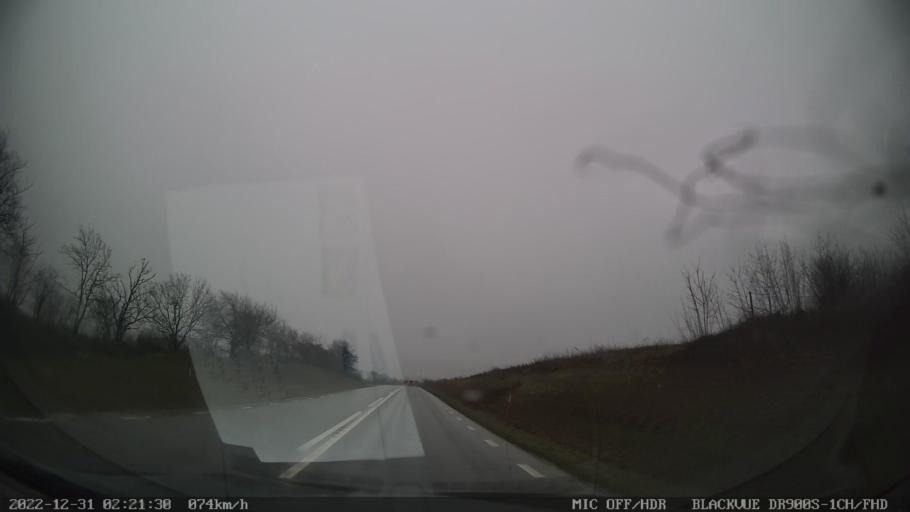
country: SE
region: Skane
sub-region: Tomelilla Kommun
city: Tomelilla
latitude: 55.5670
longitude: 14.1129
